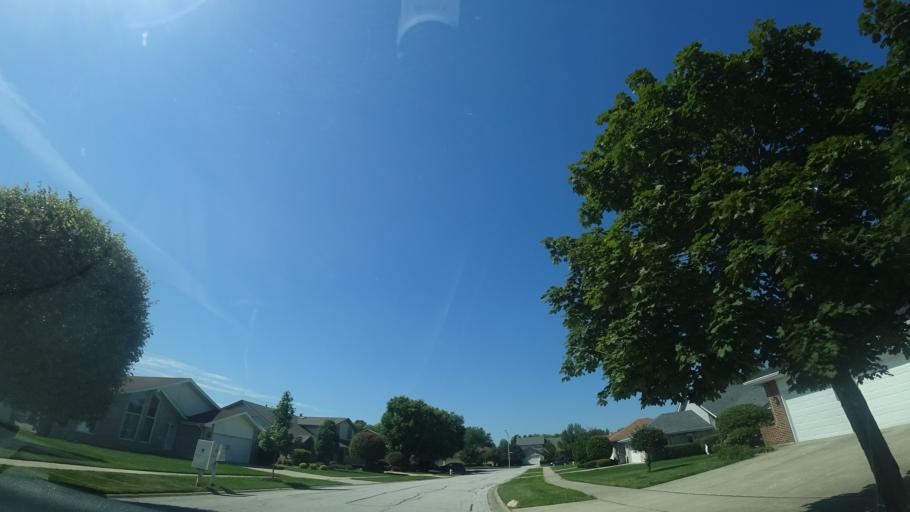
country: US
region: Illinois
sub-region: Will County
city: Homer Glen
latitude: 41.5719
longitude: -87.9059
